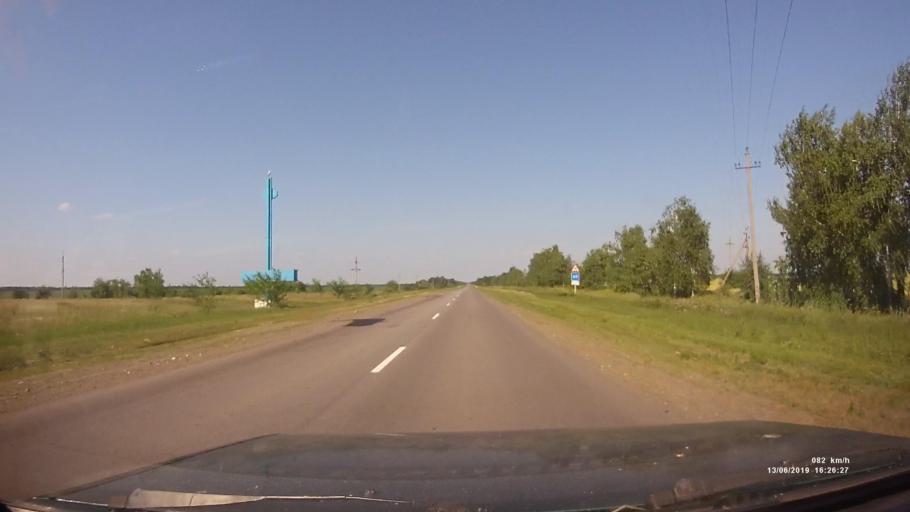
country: RU
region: Rostov
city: Kazanskaya
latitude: 49.8051
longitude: 41.1659
